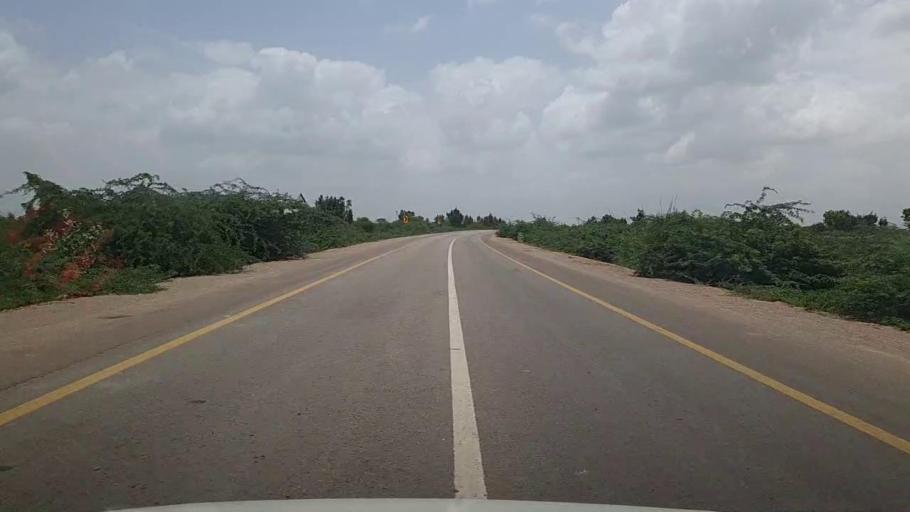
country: PK
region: Sindh
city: Thatta
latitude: 24.7425
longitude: 67.9493
